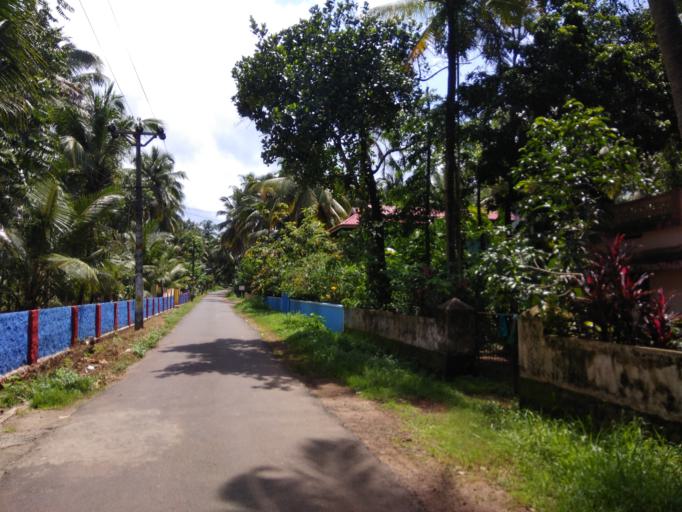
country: IN
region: Kerala
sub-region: Thrissur District
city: Avanoor
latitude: 10.5454
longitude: 76.1551
